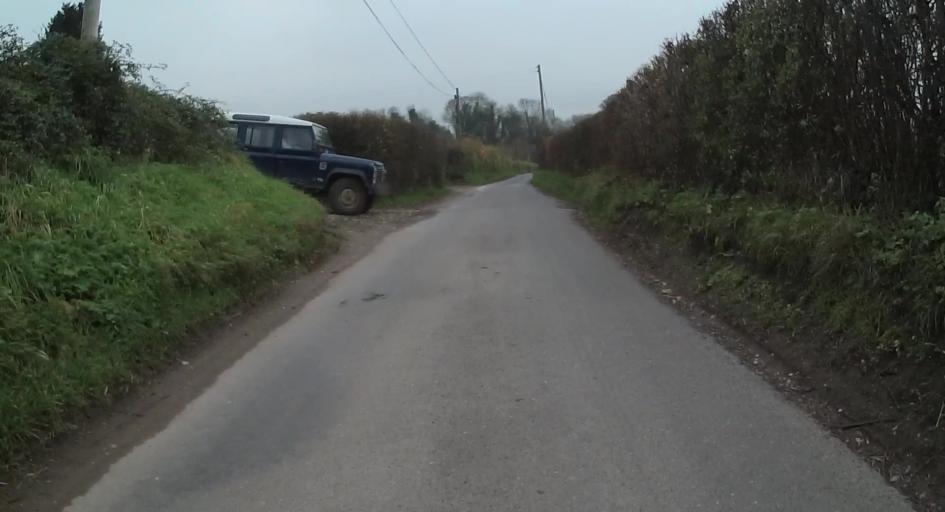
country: GB
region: England
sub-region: Hampshire
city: Kings Worthy
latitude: 51.0972
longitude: -1.2368
